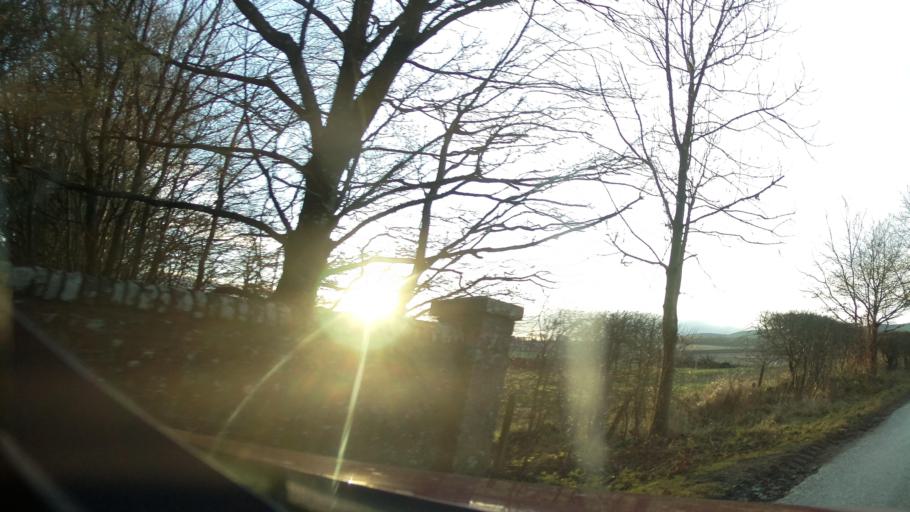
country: GB
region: Scotland
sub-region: Angus
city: Forfar
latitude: 56.5874
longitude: -2.8858
